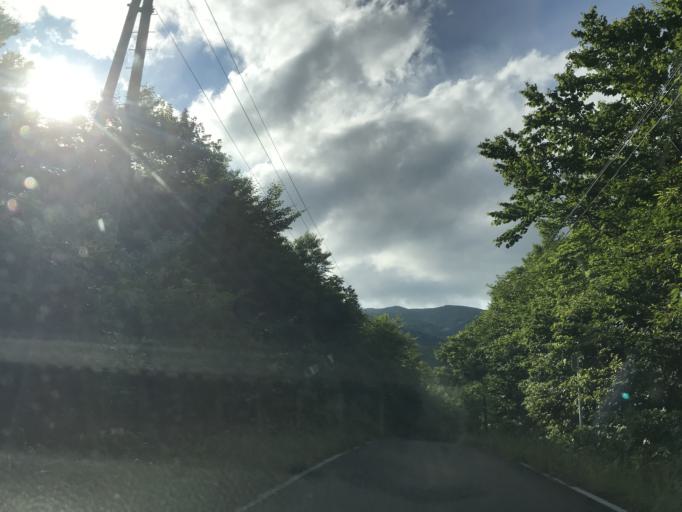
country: JP
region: Iwate
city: Ichinoseki
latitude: 38.9286
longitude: 140.8324
